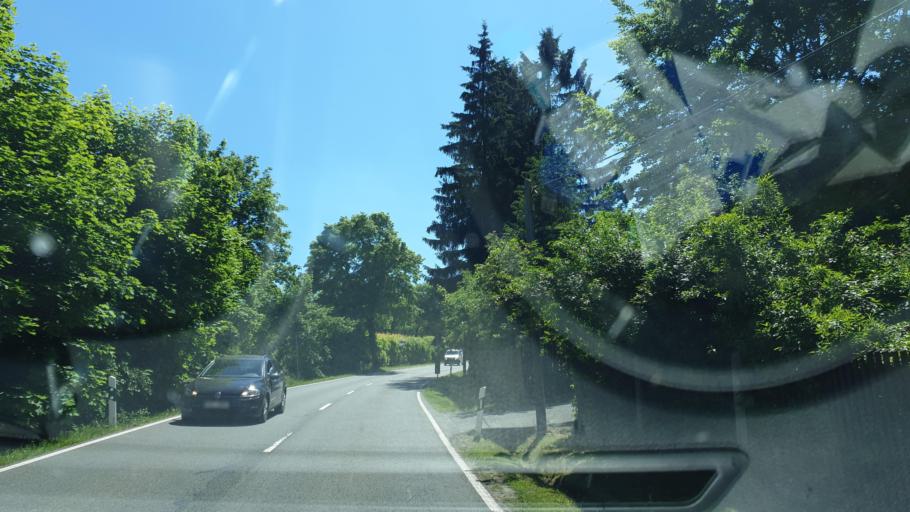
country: DE
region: Saxony
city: Falkenstein
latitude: 50.4670
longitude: 12.3672
